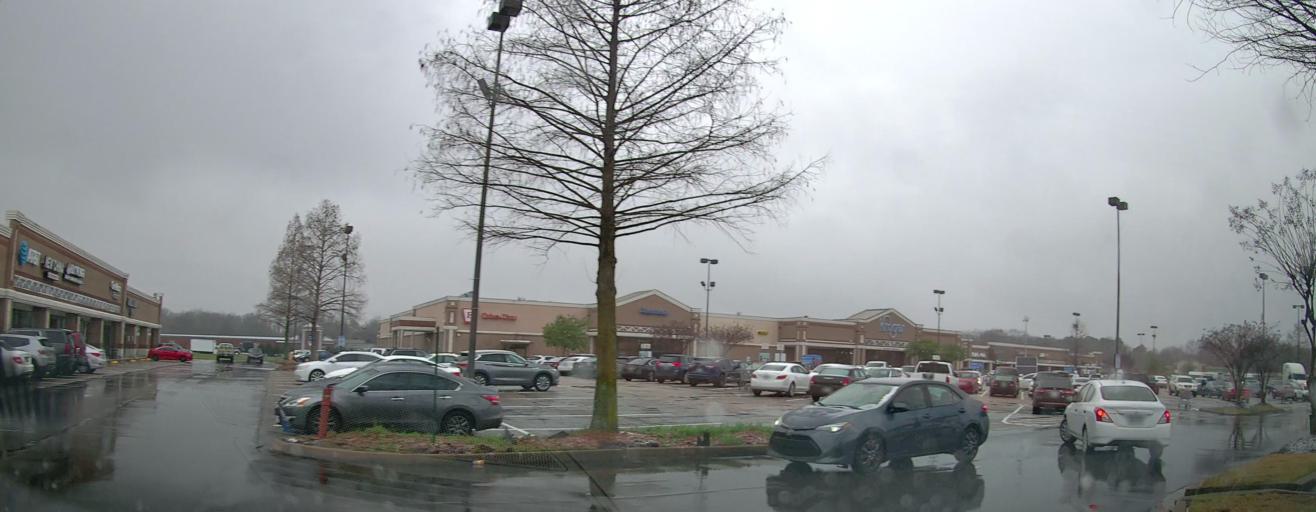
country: US
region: Tennessee
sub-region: Shelby County
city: Germantown
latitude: 35.0711
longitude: -89.8432
